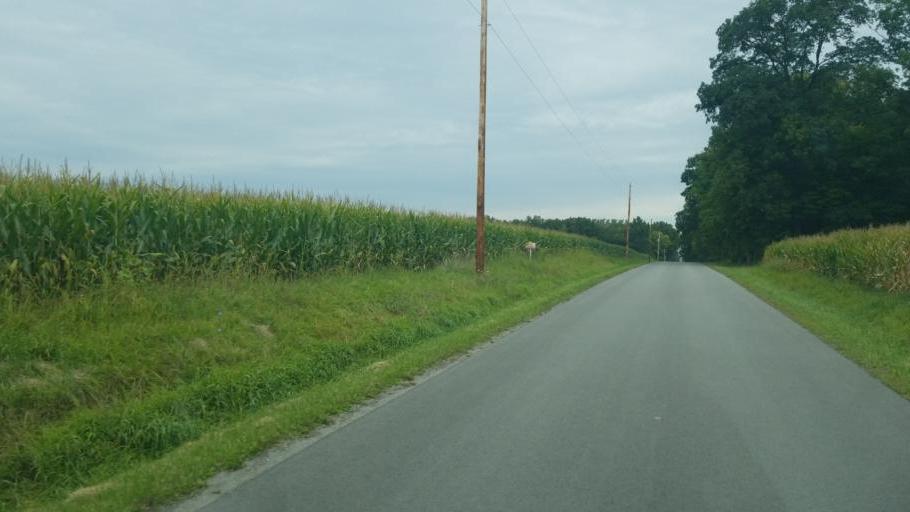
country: US
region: Ohio
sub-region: Wyandot County
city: Upper Sandusky
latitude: 40.7715
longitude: -83.1883
